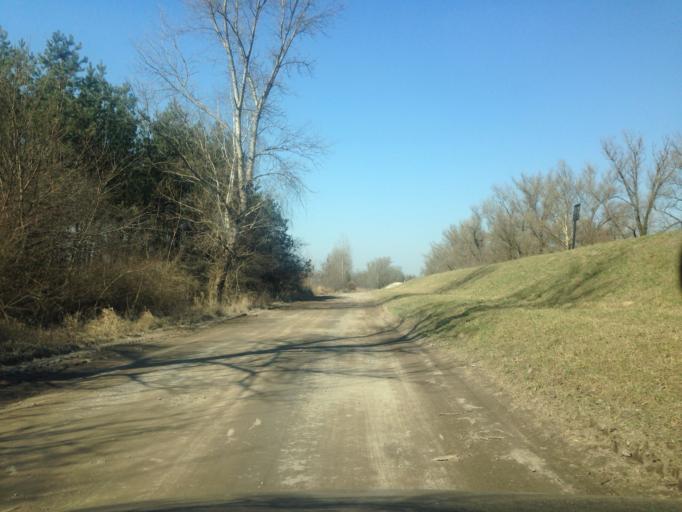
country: PL
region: Masovian Voivodeship
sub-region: Warszawa
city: Wawer
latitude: 52.1419
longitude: 21.1563
